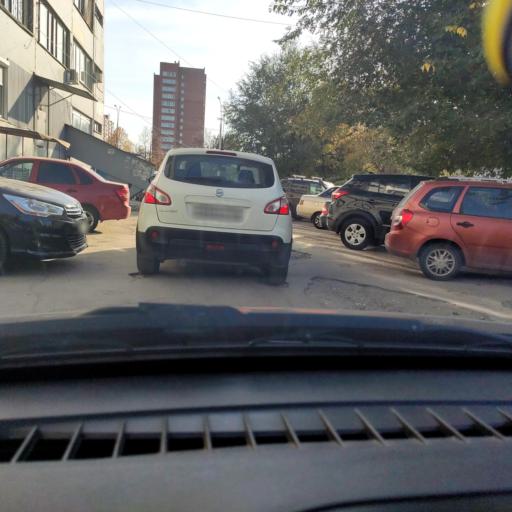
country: RU
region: Samara
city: Tol'yatti
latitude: 53.5188
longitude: 49.3045
